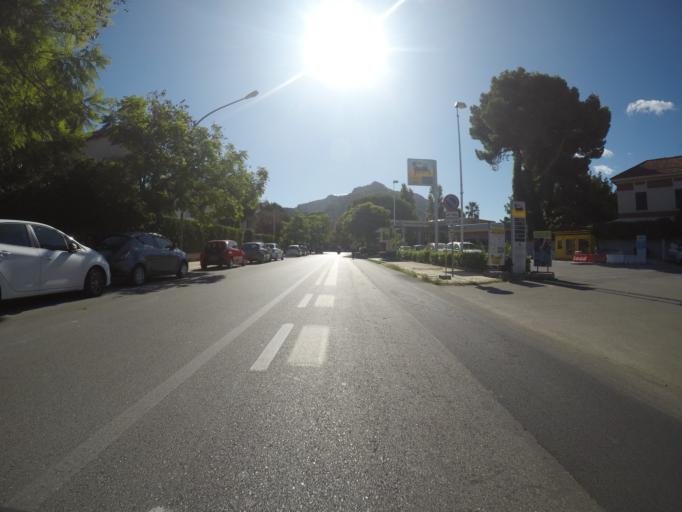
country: IT
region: Sicily
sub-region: Palermo
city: Palermo
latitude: 38.1982
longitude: 13.3287
